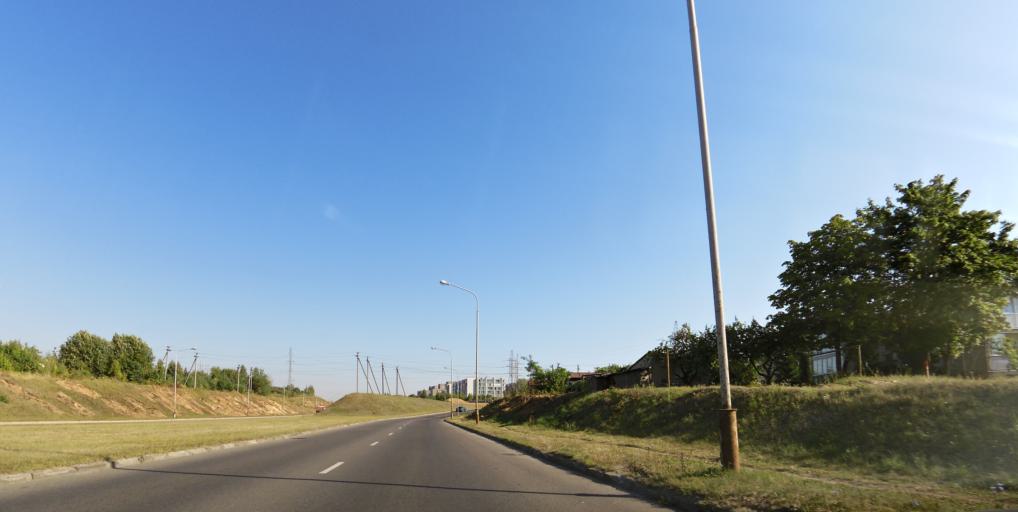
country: LT
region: Vilnius County
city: Justiniskes
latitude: 54.7039
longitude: 25.2099
